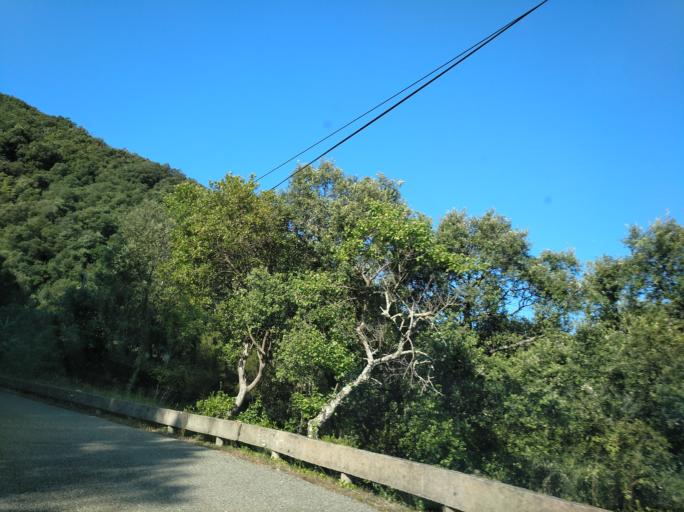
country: ES
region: Catalonia
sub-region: Provincia de Girona
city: Susqueda
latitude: 41.9832
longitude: 2.5347
